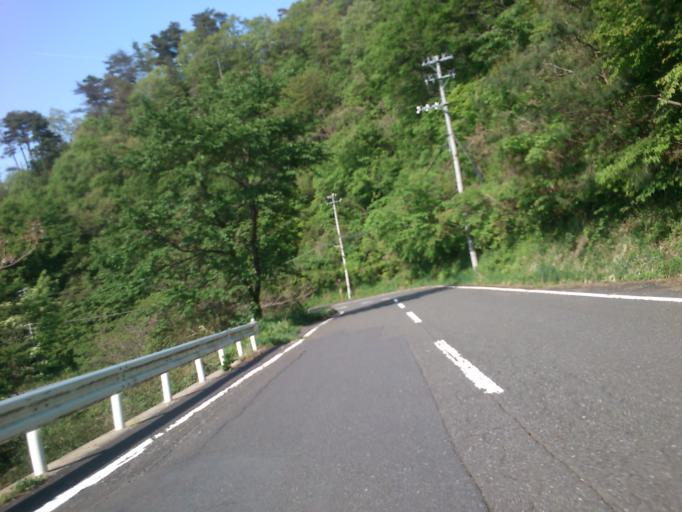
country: JP
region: Kyoto
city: Miyazu
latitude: 35.7331
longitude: 135.1765
